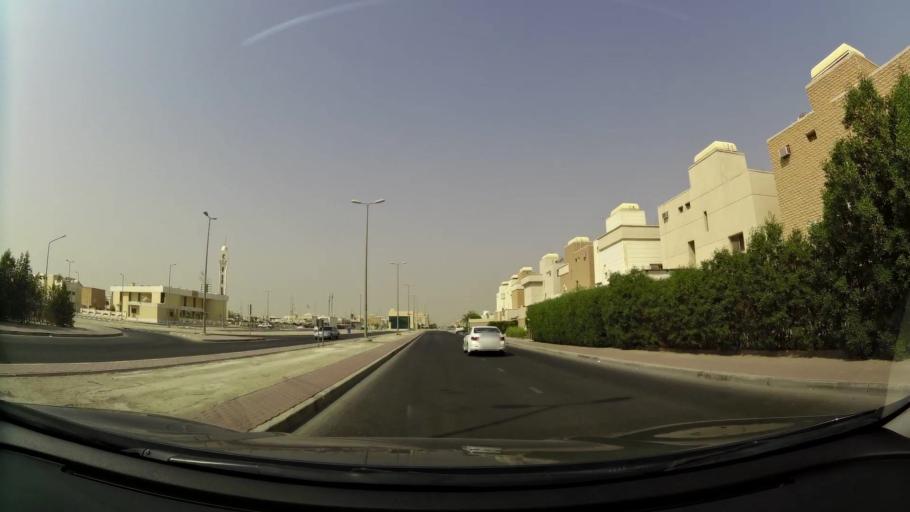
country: KW
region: Muhafazat al Jahra'
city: Al Jahra'
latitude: 29.3194
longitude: 47.7269
